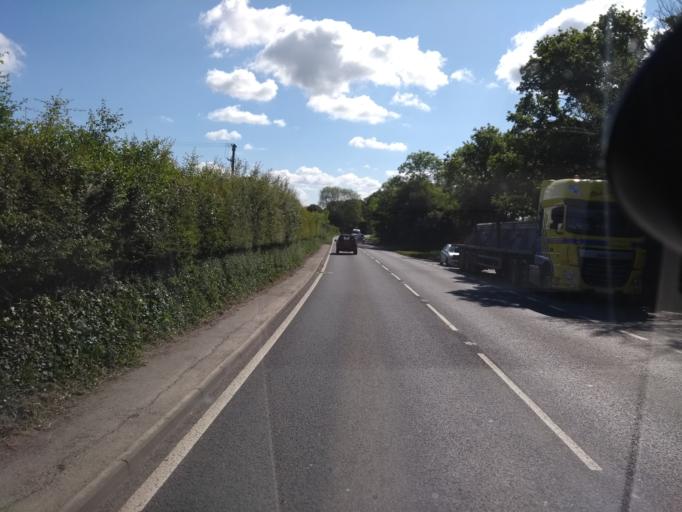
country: GB
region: England
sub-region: Somerset
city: Bridgwater
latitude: 51.1296
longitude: -3.0362
